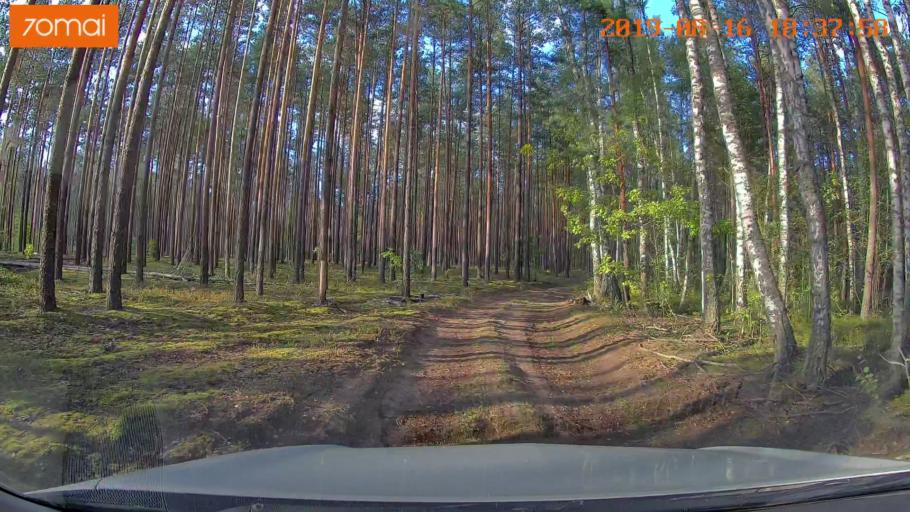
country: BY
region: Mogilev
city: Asipovichy
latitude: 53.2092
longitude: 28.6346
